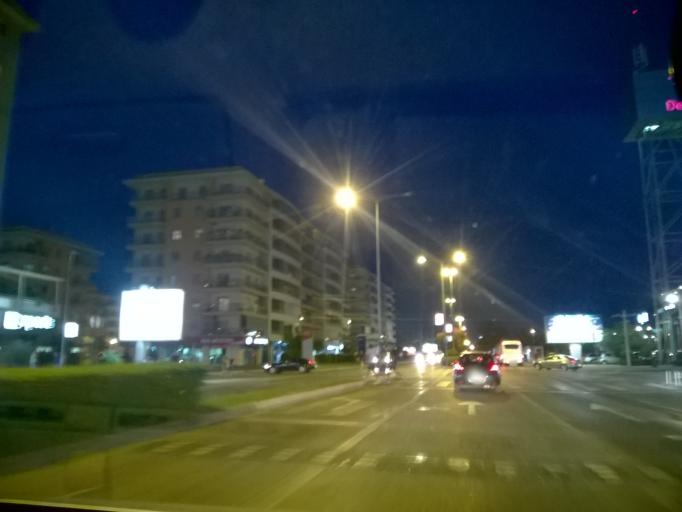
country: ME
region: Podgorica
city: Podgorica
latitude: 42.4379
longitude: 19.2349
